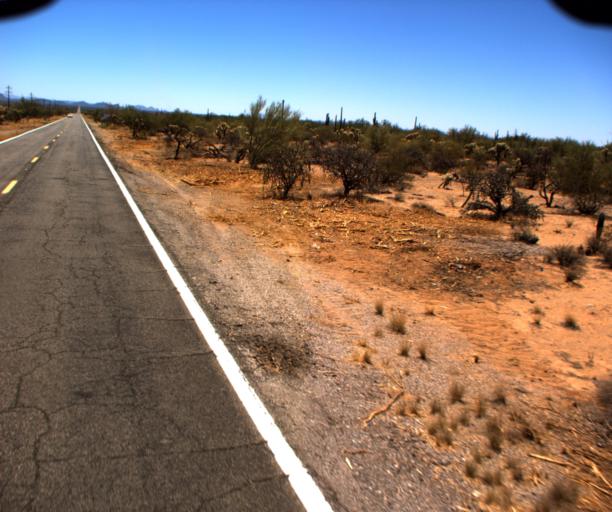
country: US
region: Arizona
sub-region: Pima County
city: Sells
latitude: 32.1145
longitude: -112.0771
